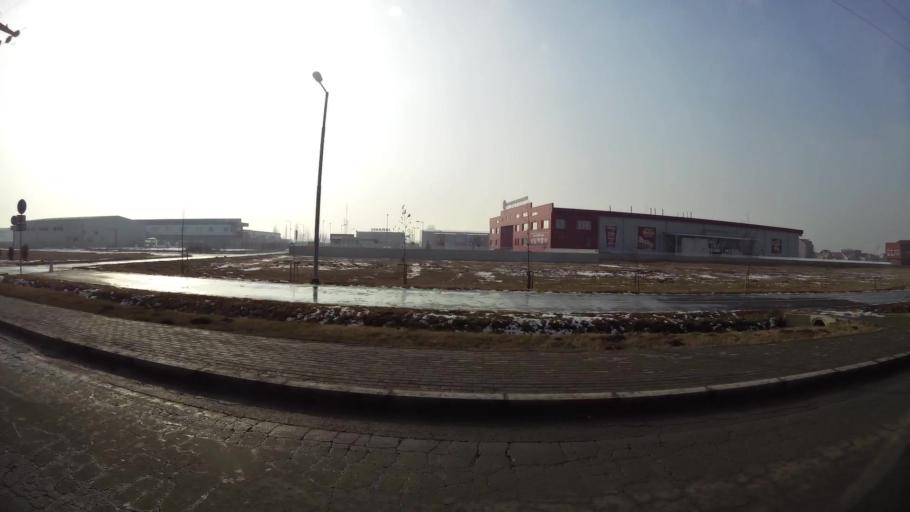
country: MK
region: Ilinden
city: Marino
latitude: 41.9850
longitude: 21.5900
